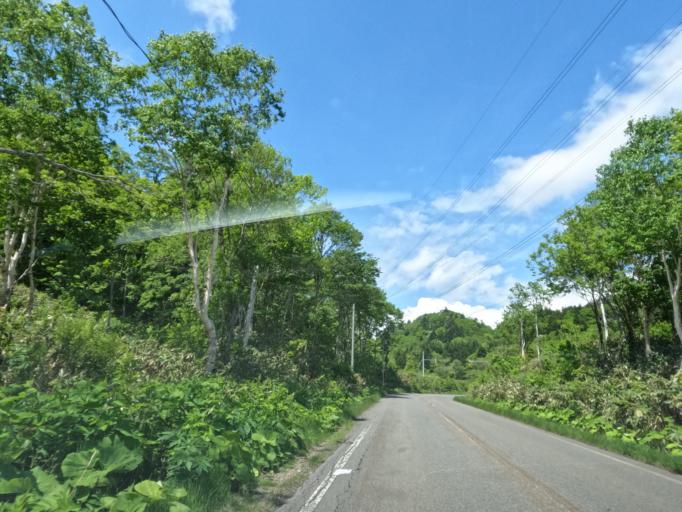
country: JP
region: Hokkaido
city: Takikawa
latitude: 43.5481
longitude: 141.6164
